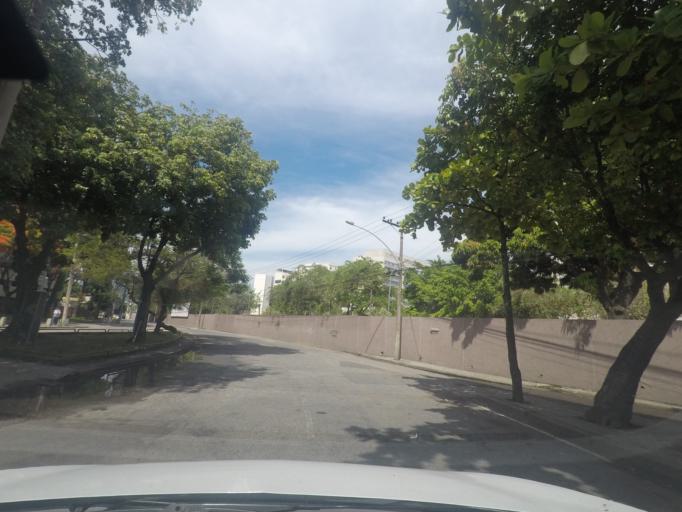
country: BR
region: Rio de Janeiro
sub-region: Rio De Janeiro
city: Rio de Janeiro
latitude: -22.9074
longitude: -43.2187
